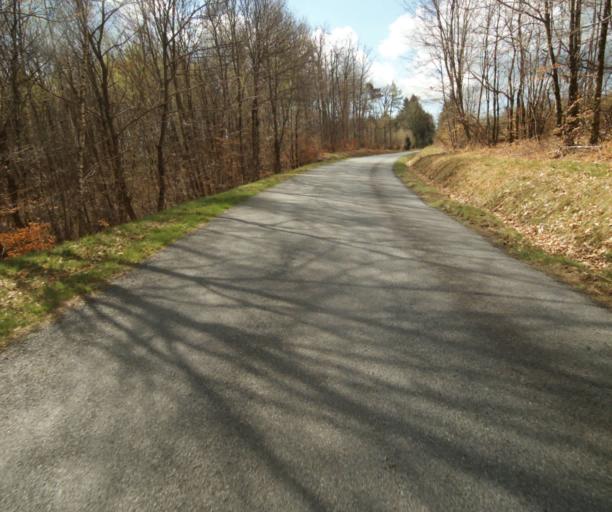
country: FR
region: Limousin
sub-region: Departement de la Correze
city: Argentat
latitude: 45.2329
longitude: 1.9355
